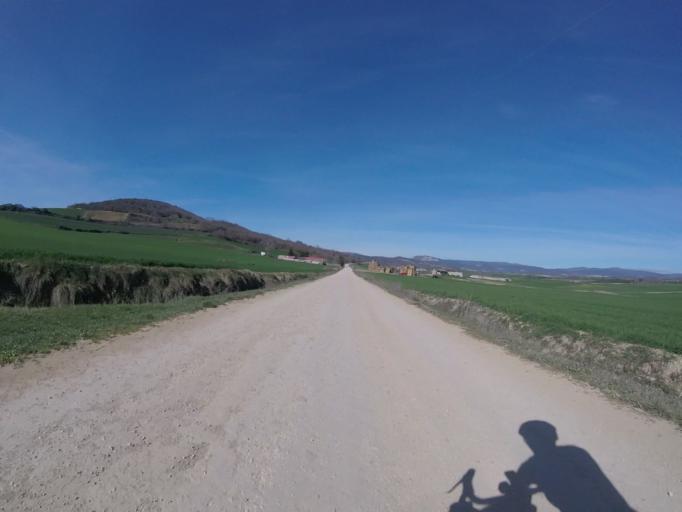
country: ES
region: Navarre
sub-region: Provincia de Navarra
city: Villatuerta
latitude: 42.6510
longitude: -1.9718
